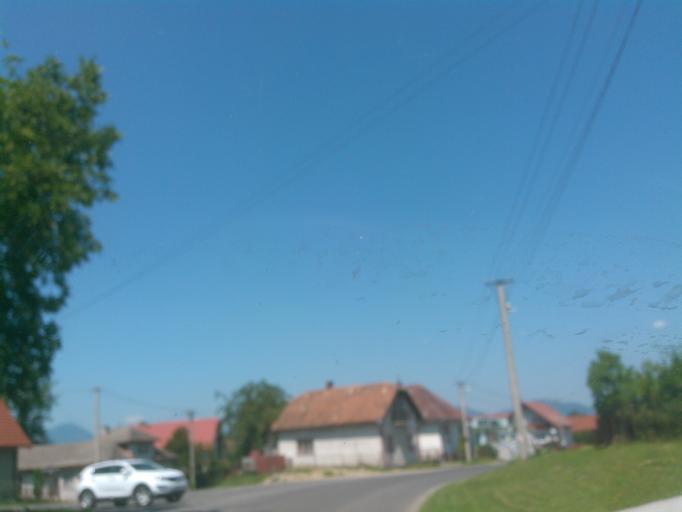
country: SK
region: Zilinsky
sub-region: Okres Liptovsky Mikulas
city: Liptovsky Mikulas
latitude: 49.0500
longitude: 19.4836
